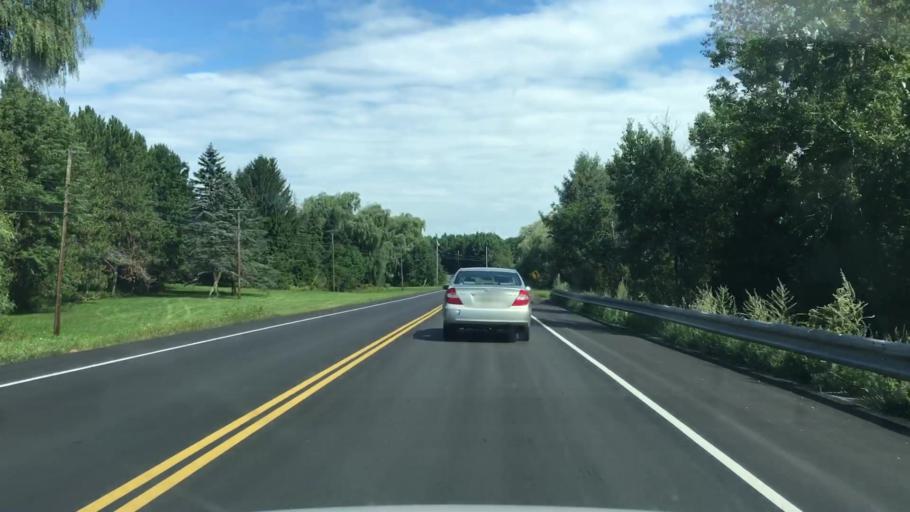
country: US
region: Maine
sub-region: Penobscot County
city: Corinna
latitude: 44.9431
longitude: -69.2472
